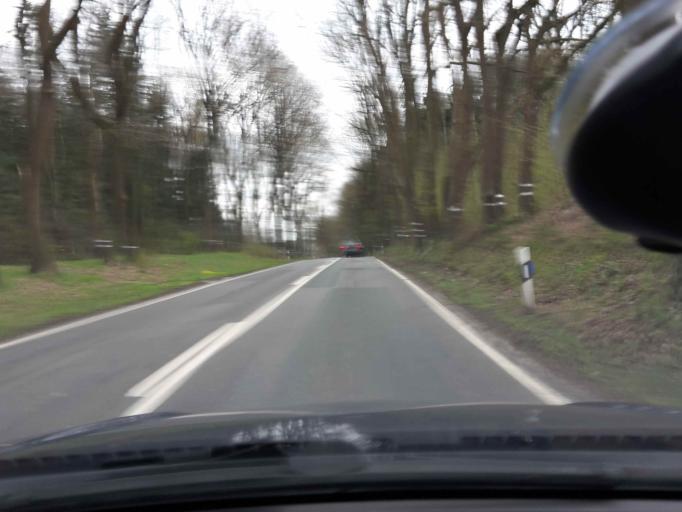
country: DE
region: Lower Saxony
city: Harmstorf
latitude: 53.3587
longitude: 9.9884
